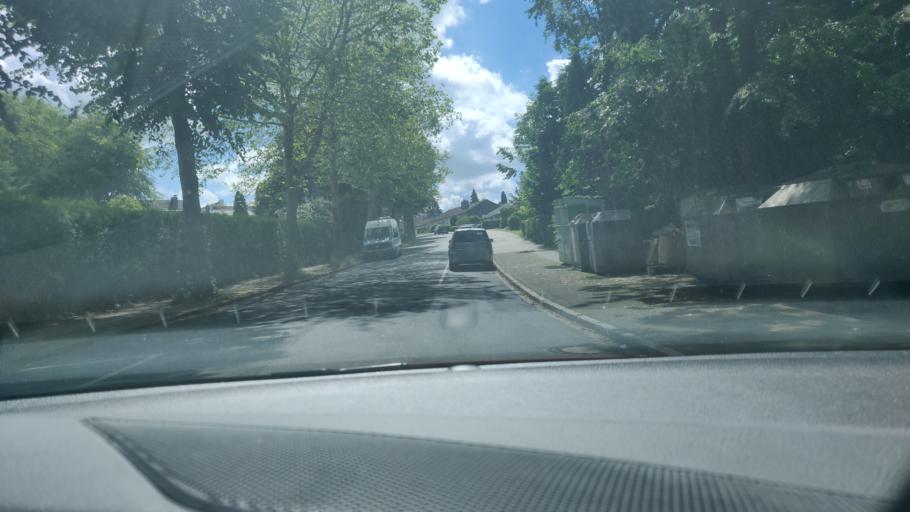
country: DE
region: North Rhine-Westphalia
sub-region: Regierungsbezirk Dusseldorf
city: Heiligenhaus
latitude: 51.3216
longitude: 6.9620
